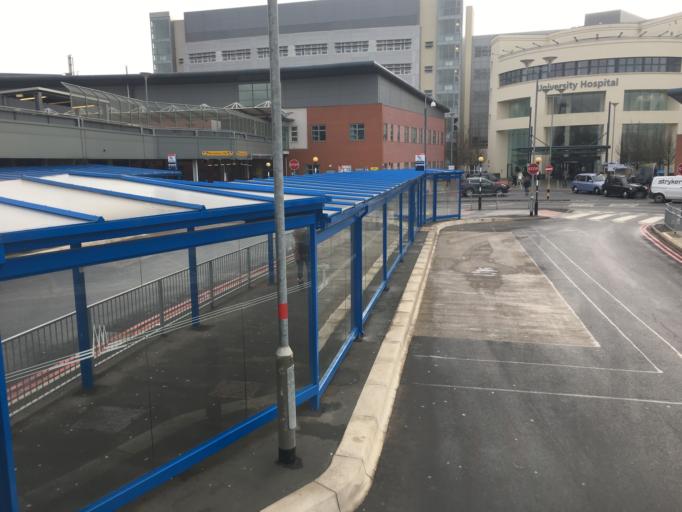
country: GB
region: England
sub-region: Warwickshire
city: Brandon
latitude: 52.4218
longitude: -1.4386
